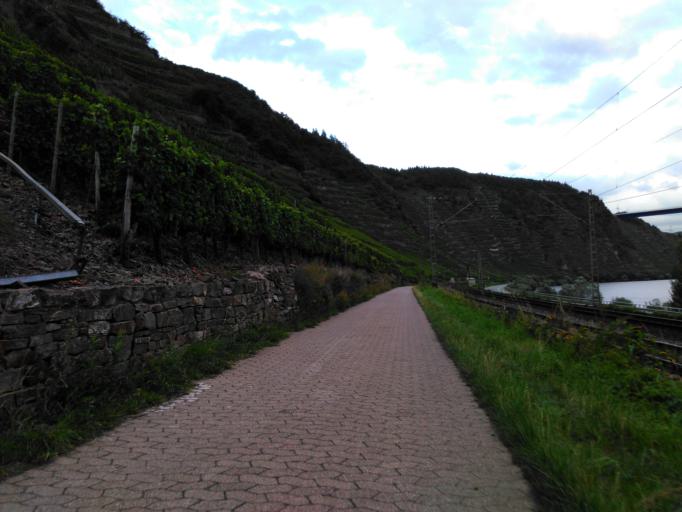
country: DE
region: Rheinland-Pfalz
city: Dieblich
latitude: 50.3219
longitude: 7.4801
